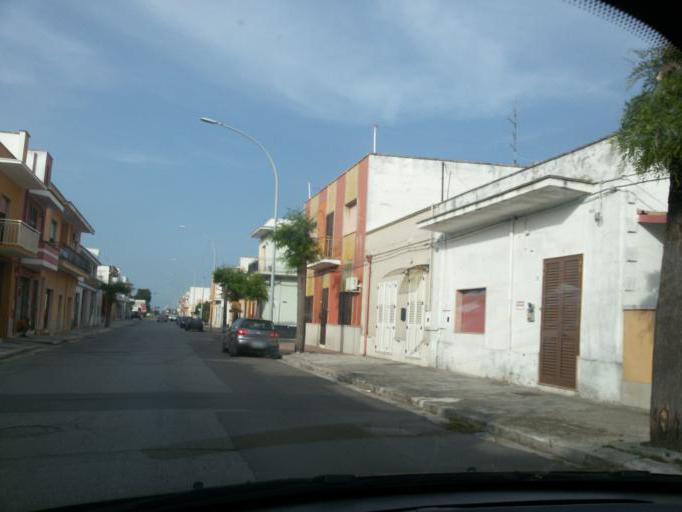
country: IT
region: Apulia
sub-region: Provincia di Brindisi
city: San Donaci
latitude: 40.4514
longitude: 17.9295
